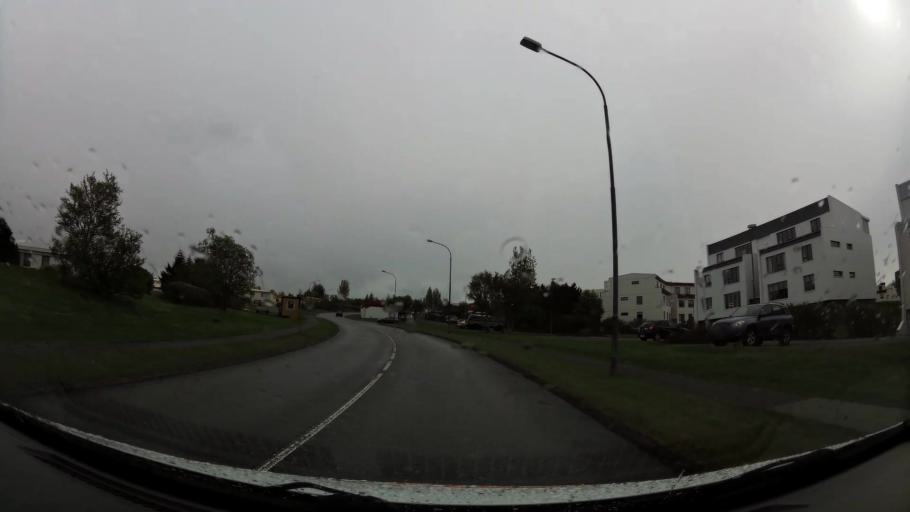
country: IS
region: Capital Region
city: Gardabaer
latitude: 64.0913
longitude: -21.9143
